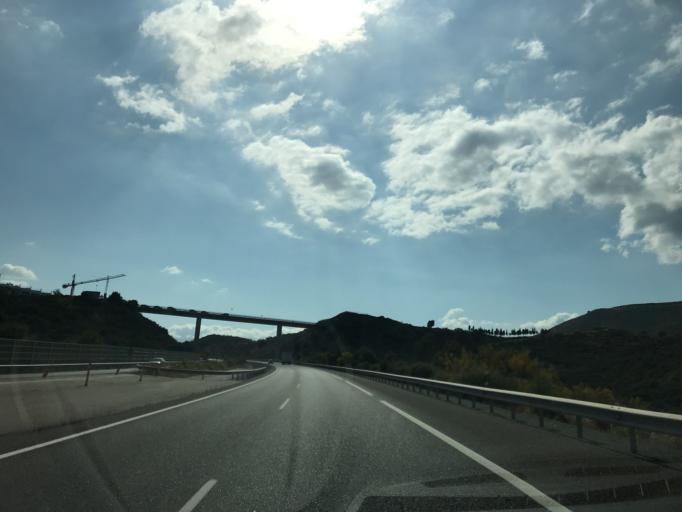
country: ES
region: Andalusia
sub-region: Provincia de Malaga
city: Istan
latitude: 36.5264
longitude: -4.9659
